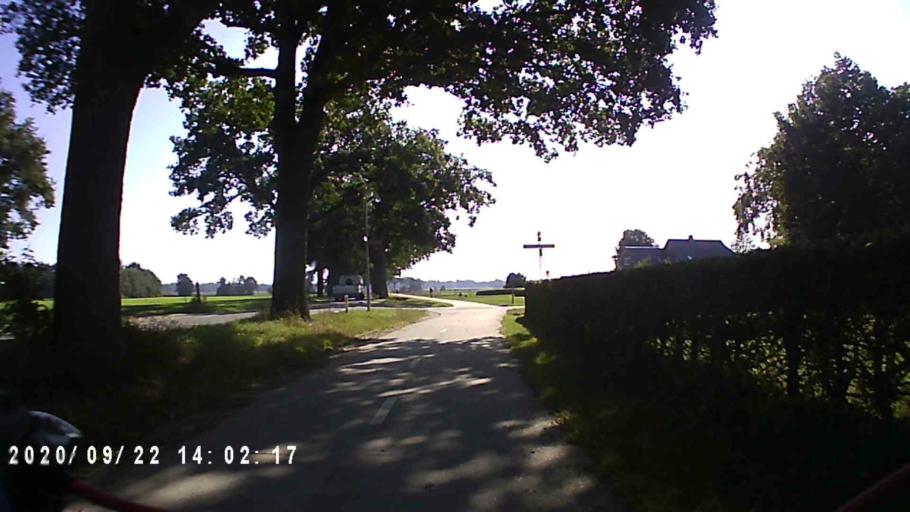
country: NL
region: Groningen
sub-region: Gemeente Leek
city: Leek
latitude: 53.1078
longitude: 6.4281
